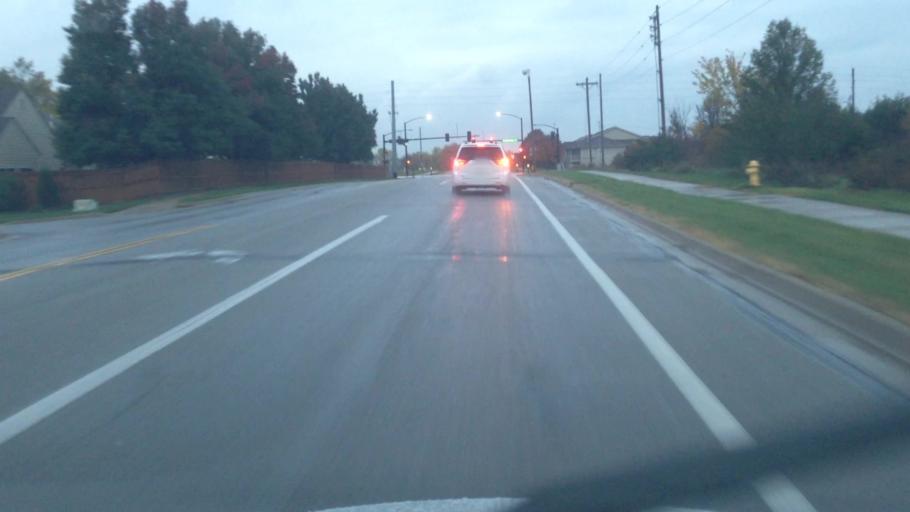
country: US
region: Kansas
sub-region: Douglas County
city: Lawrence
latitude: 38.9611
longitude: -95.3257
